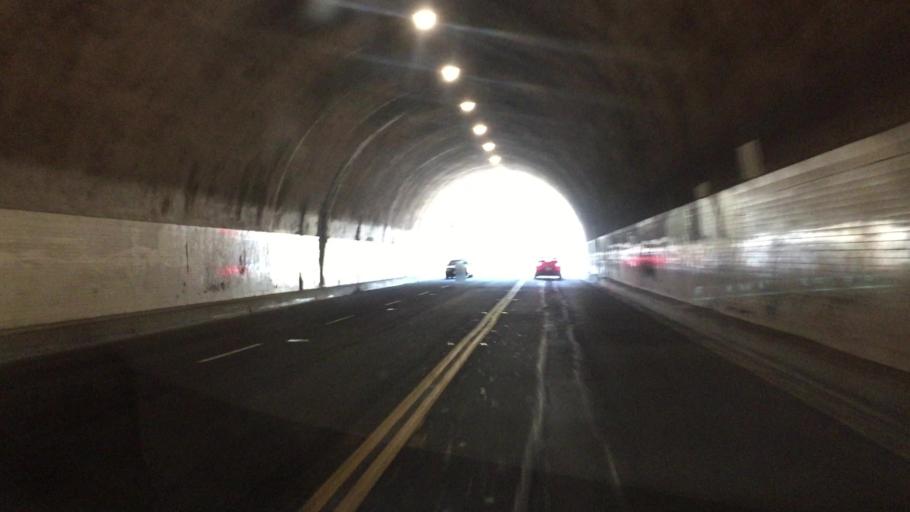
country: US
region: California
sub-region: Los Angeles County
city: Sherman Oaks
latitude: 34.1298
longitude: -118.4805
